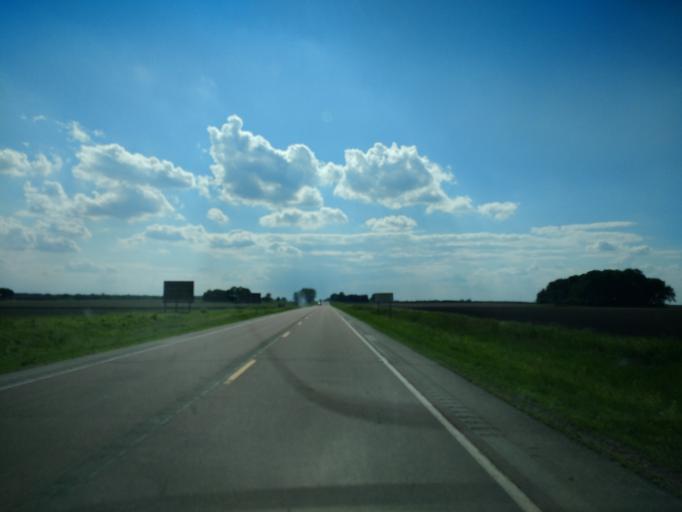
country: US
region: Iowa
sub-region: Clay County
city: Spencer
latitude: 43.1840
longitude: -95.1569
